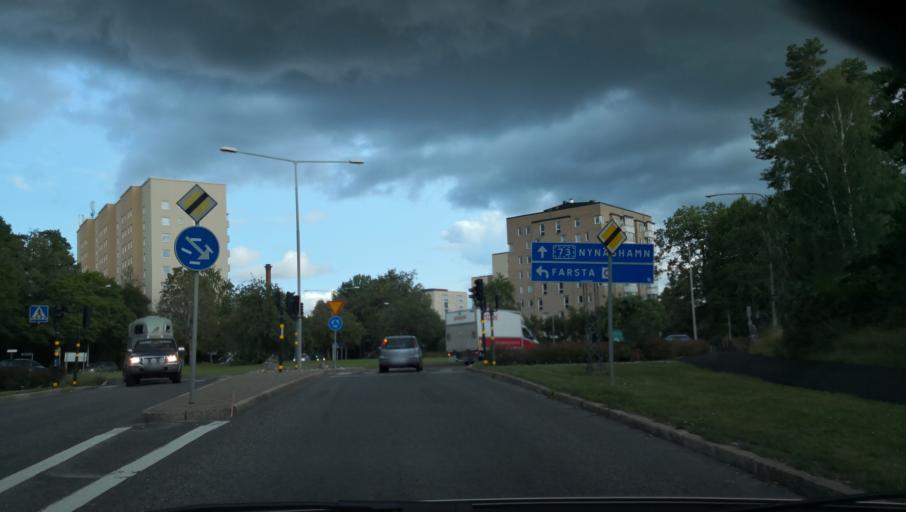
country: SE
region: Stockholm
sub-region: Stockholms Kommun
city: Arsta
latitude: 59.2383
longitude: 18.0914
